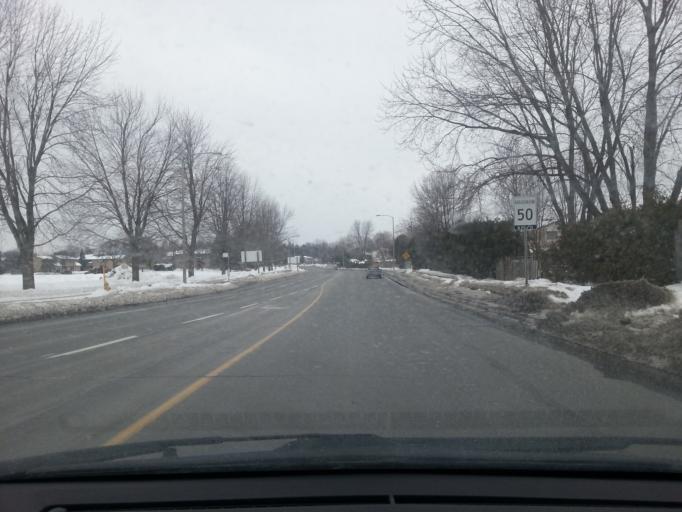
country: CA
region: Quebec
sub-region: Outaouais
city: Gatineau
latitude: 45.4843
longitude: -75.5207
